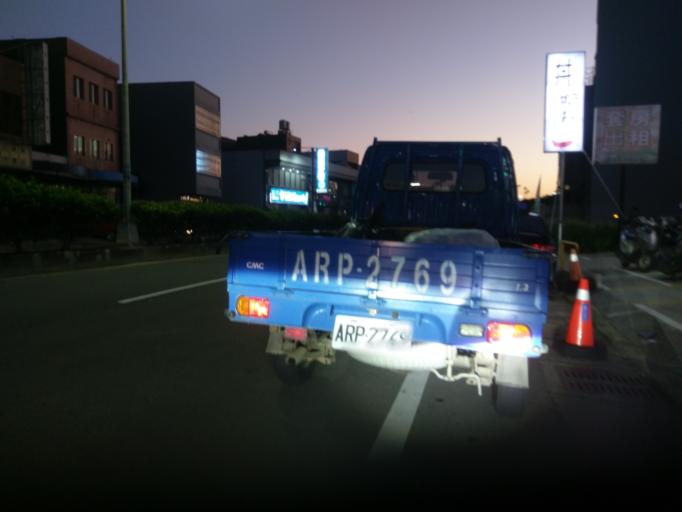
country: TW
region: Taiwan
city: Taoyuan City
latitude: 25.0443
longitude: 121.1391
